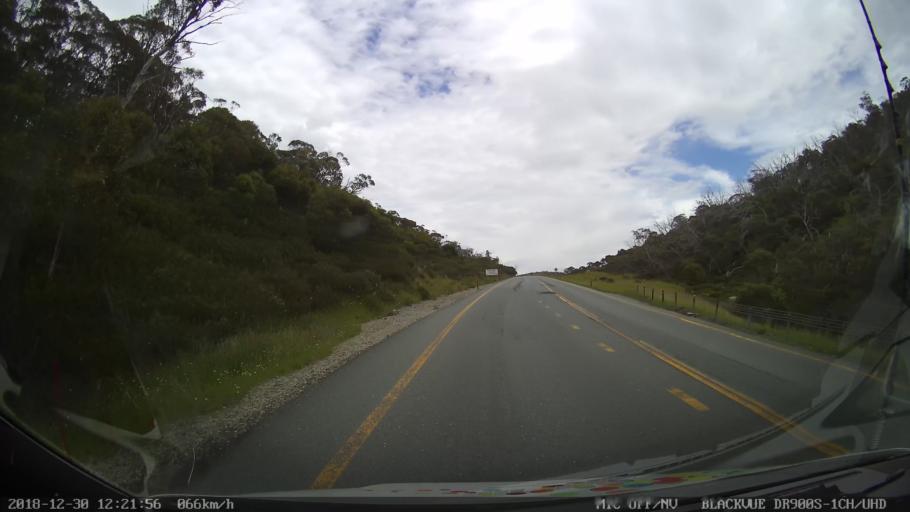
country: AU
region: New South Wales
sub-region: Snowy River
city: Jindabyne
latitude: -36.3556
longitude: 148.5144
